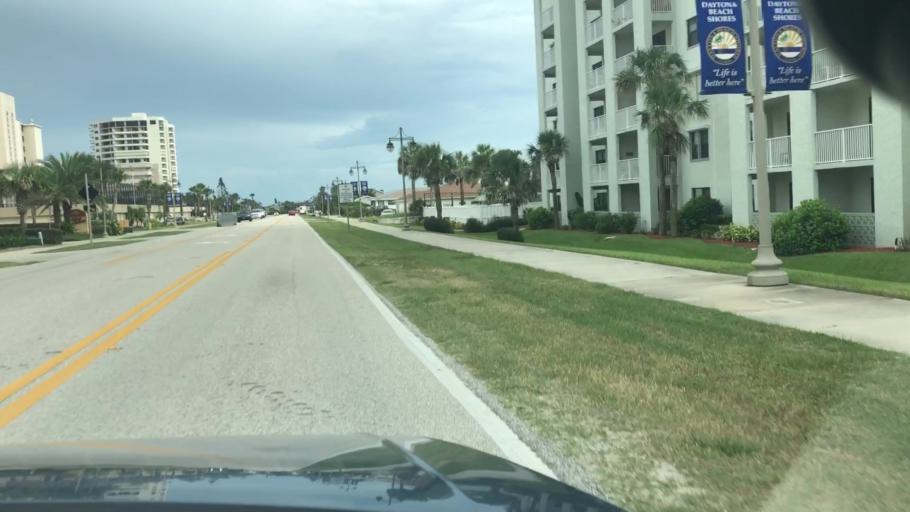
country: US
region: Florida
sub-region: Volusia County
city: Port Orange
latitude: 29.1410
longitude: -80.9636
